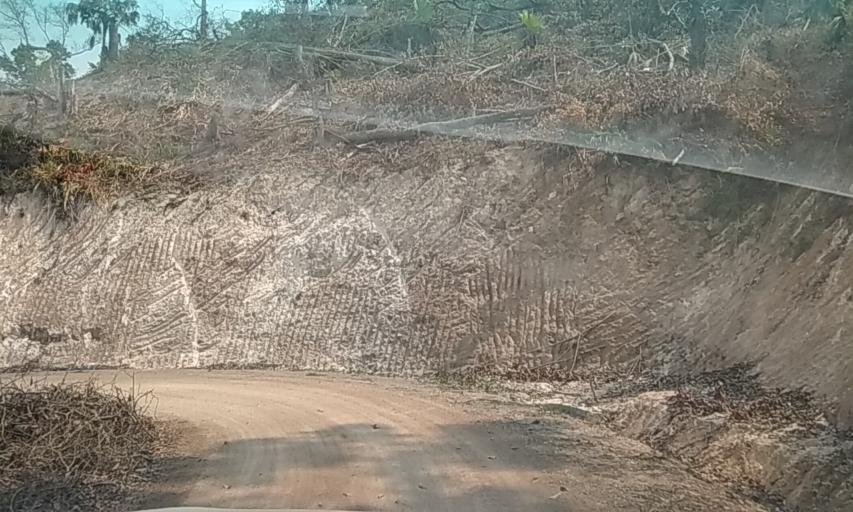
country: VN
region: Huyen Dien Bien
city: Dien Bien Phu
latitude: 21.4863
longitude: 102.7833
